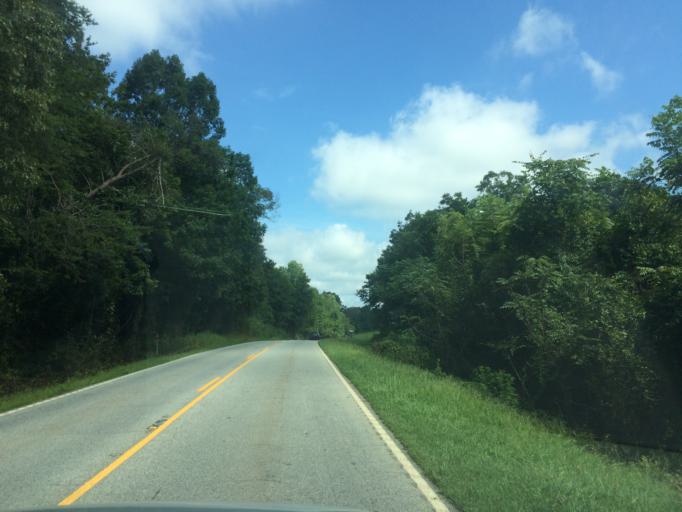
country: US
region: South Carolina
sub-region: Spartanburg County
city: Inman Mills
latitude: 35.0001
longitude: -82.1121
